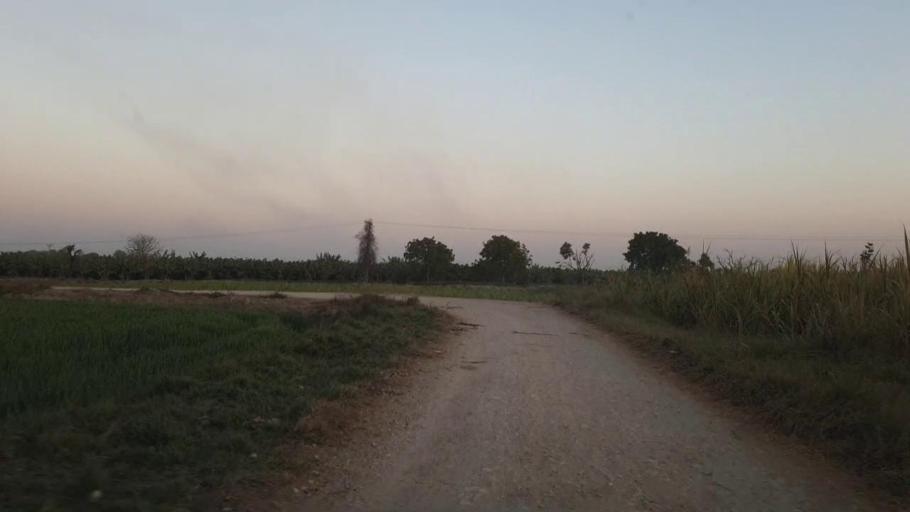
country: PK
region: Sindh
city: Chambar
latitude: 25.3409
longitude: 68.7518
